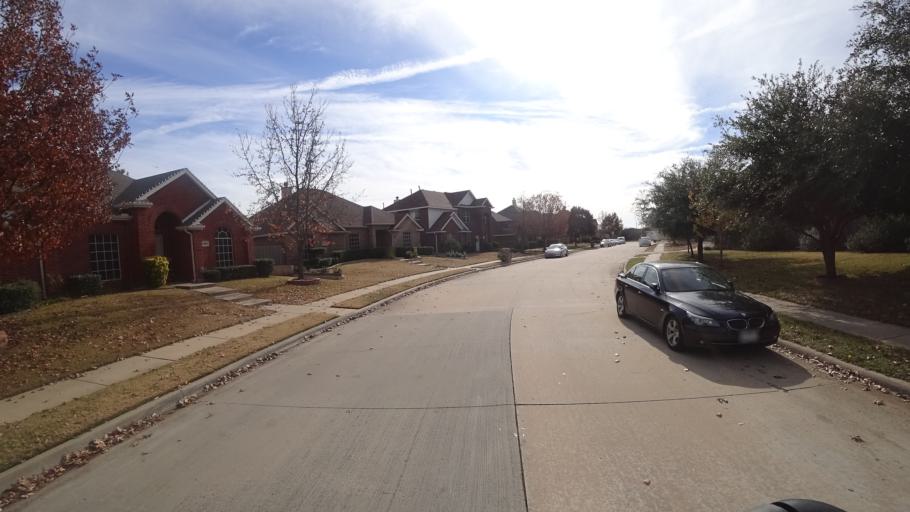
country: US
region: Texas
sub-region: Denton County
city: Highland Village
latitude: 33.0636
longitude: -97.0317
